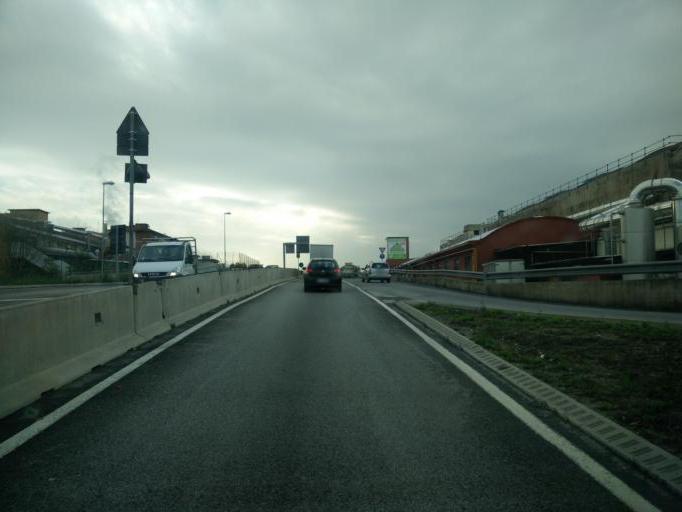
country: IT
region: Tuscany
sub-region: Provincia di Prato
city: Prato
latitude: 43.8725
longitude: 11.0830
